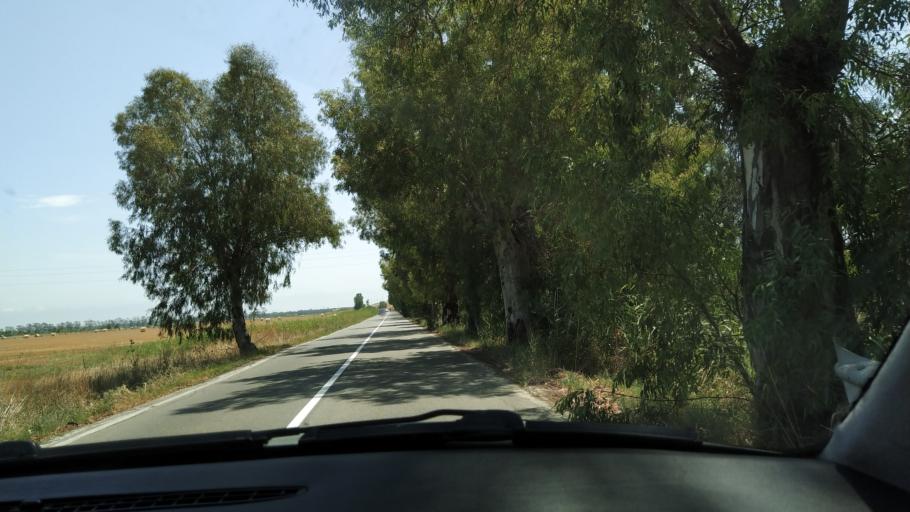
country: IT
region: Basilicate
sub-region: Provincia di Matera
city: Marconia
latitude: 40.3384
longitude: 16.7675
